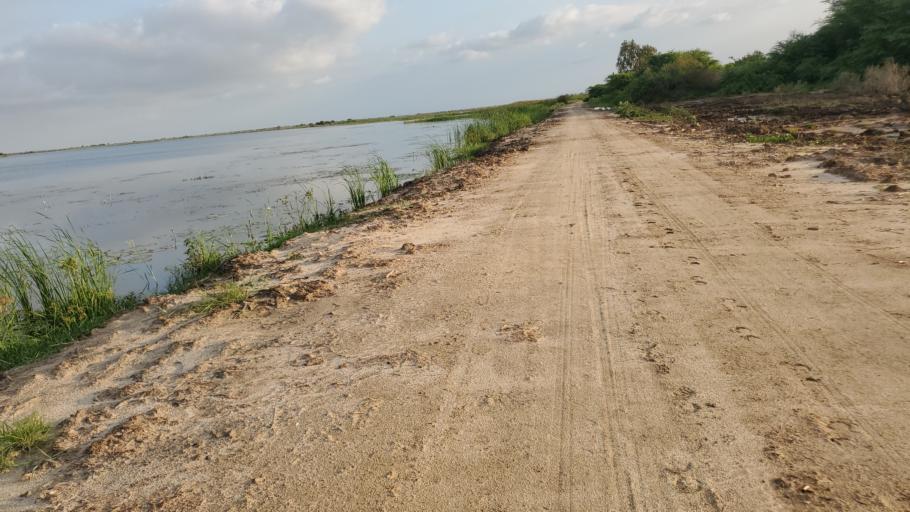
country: SN
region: Saint-Louis
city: Saint-Louis
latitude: 16.0409
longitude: -16.4168
